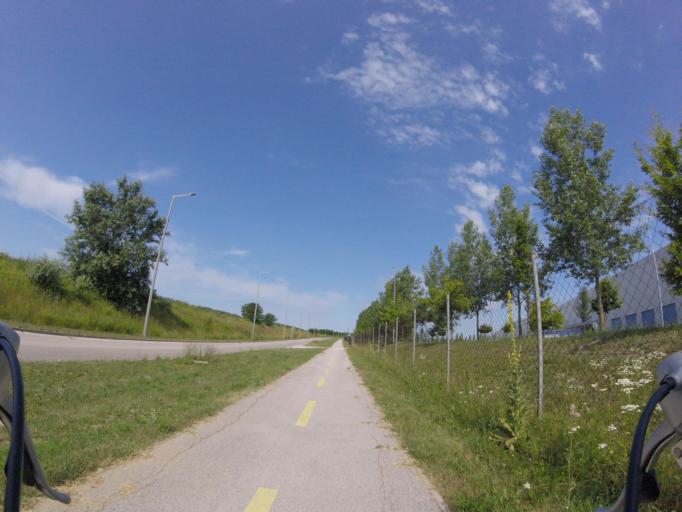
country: HU
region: Komarom-Esztergom
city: Kornye
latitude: 47.5859
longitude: 18.3267
